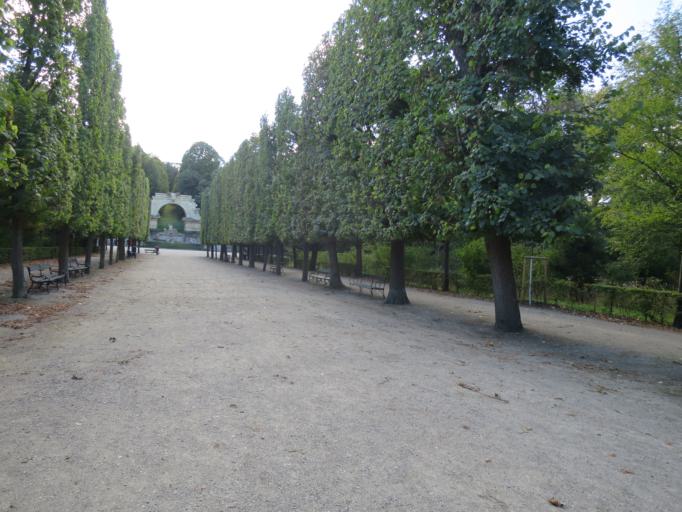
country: AT
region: Vienna
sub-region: Wien Stadt
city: Vienna
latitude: 48.1819
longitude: 16.3140
